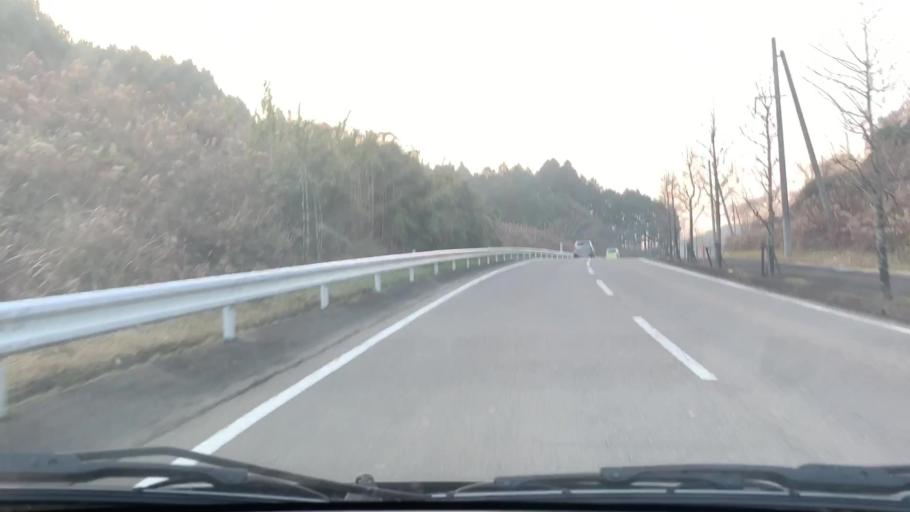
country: JP
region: Saga Prefecture
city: Imaricho-ko
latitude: 33.2592
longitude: 129.9237
